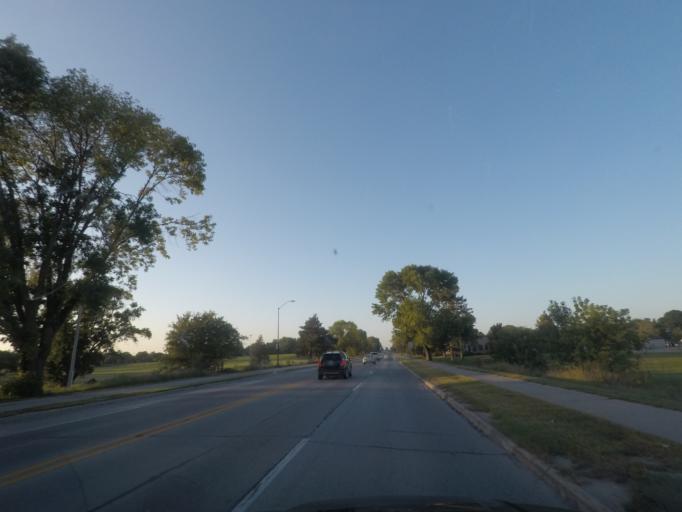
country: US
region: Iowa
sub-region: Story County
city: Ames
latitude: 42.0382
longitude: -93.6448
